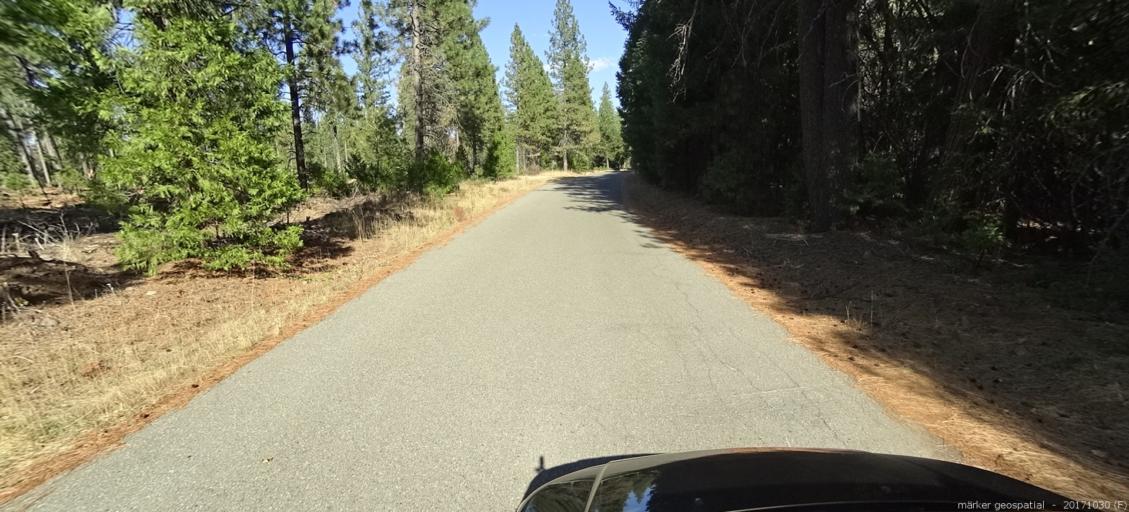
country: US
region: California
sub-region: Shasta County
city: Shingletown
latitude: 40.5103
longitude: -121.7340
